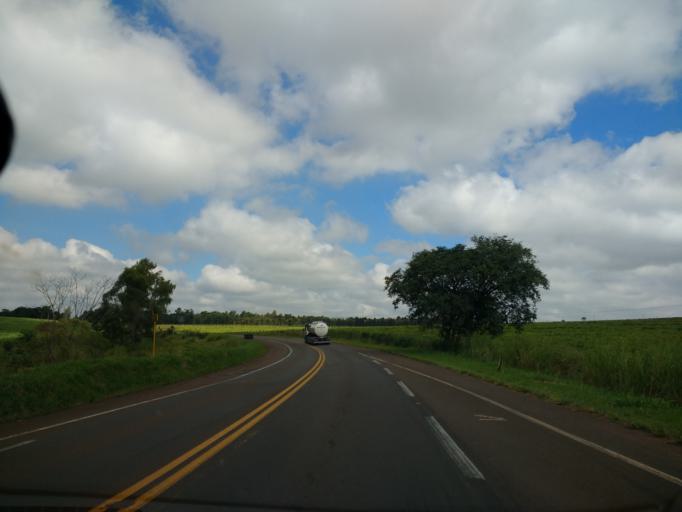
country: BR
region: Parana
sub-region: Cruzeiro Do Oeste
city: Cruzeiro do Oeste
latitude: -23.7748
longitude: -53.0234
